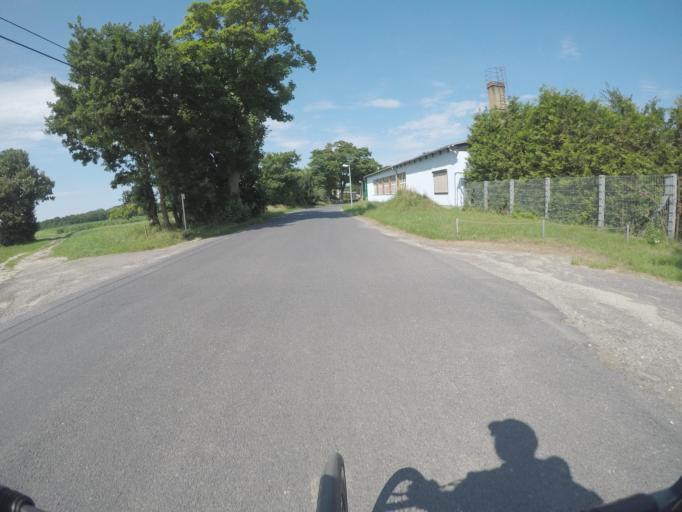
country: DE
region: Mecklenburg-Vorpommern
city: Gingst
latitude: 54.4373
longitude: 13.2221
